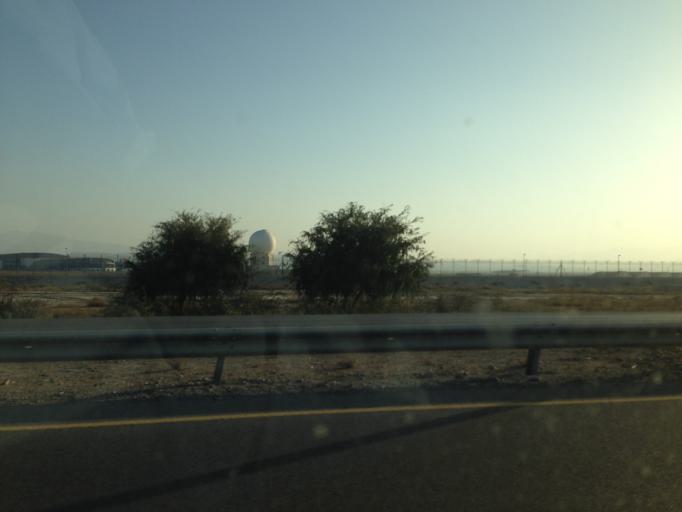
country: OM
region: Muhafazat Masqat
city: As Sib al Jadidah
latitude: 23.6157
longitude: 58.2884
